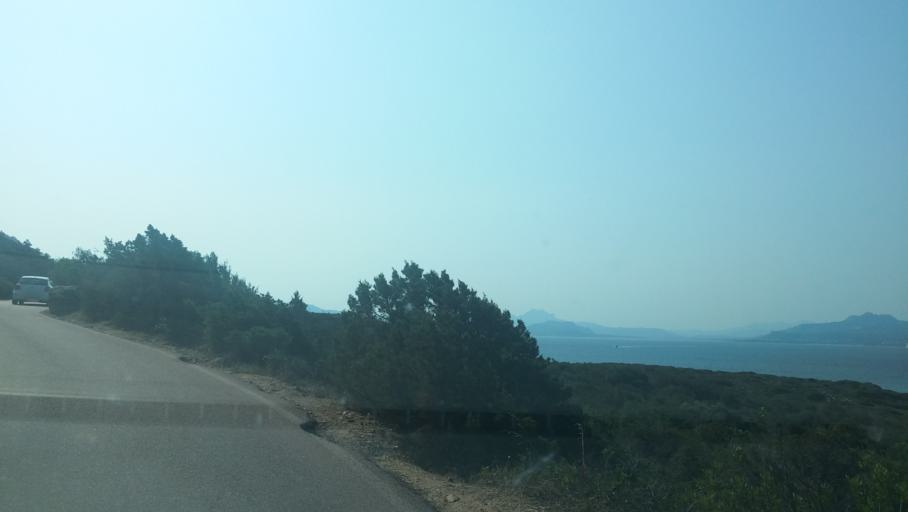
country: IT
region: Sardinia
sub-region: Provincia di Olbia-Tempio
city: La Maddalena
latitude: 41.1842
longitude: 9.4574
